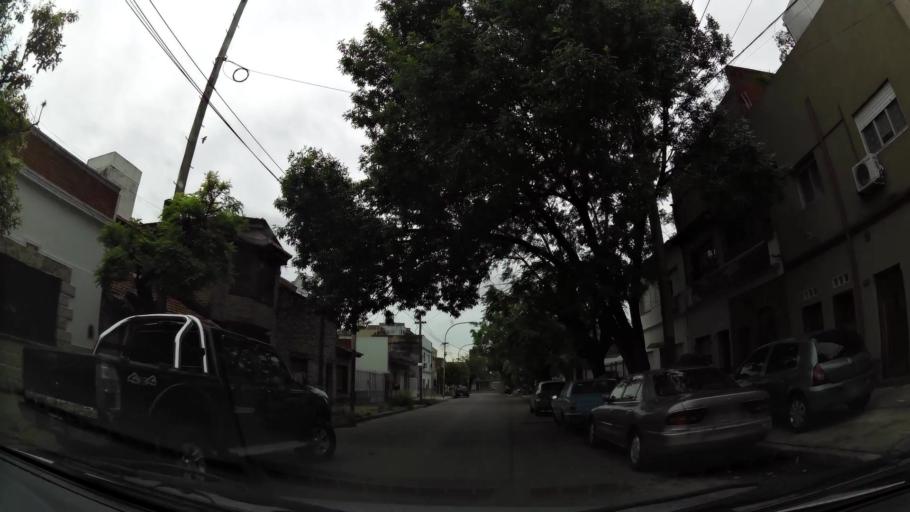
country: AR
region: Buenos Aires
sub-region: Partido de Lanus
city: Lanus
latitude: -34.6995
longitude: -58.3815
